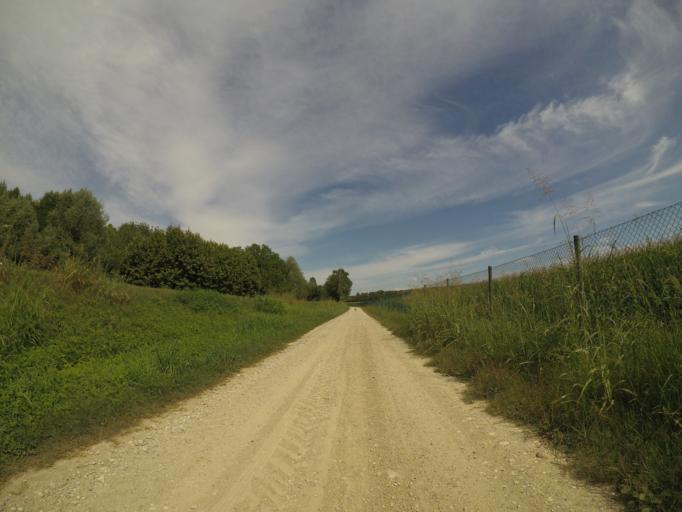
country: IT
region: Friuli Venezia Giulia
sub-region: Provincia di Udine
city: Varmo
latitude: 45.9223
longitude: 13.0139
